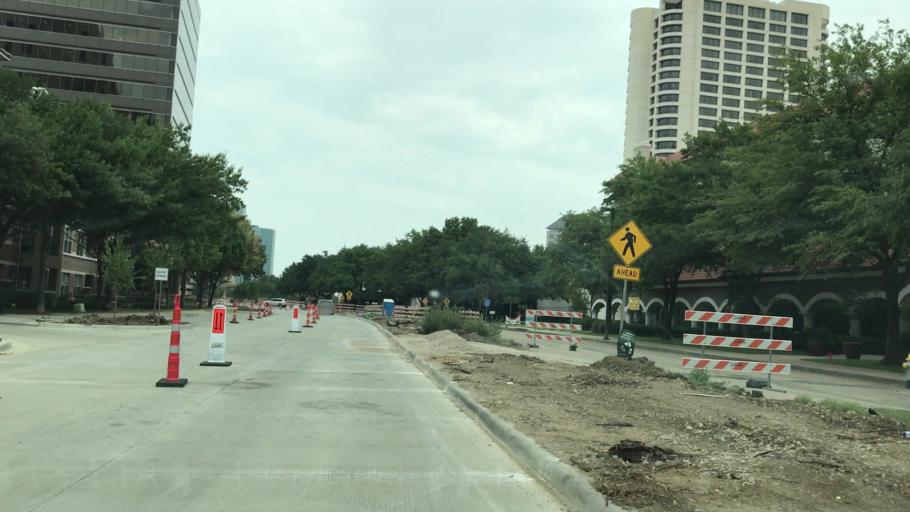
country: US
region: Texas
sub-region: Dallas County
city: Irving
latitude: 32.8658
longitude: -96.9376
